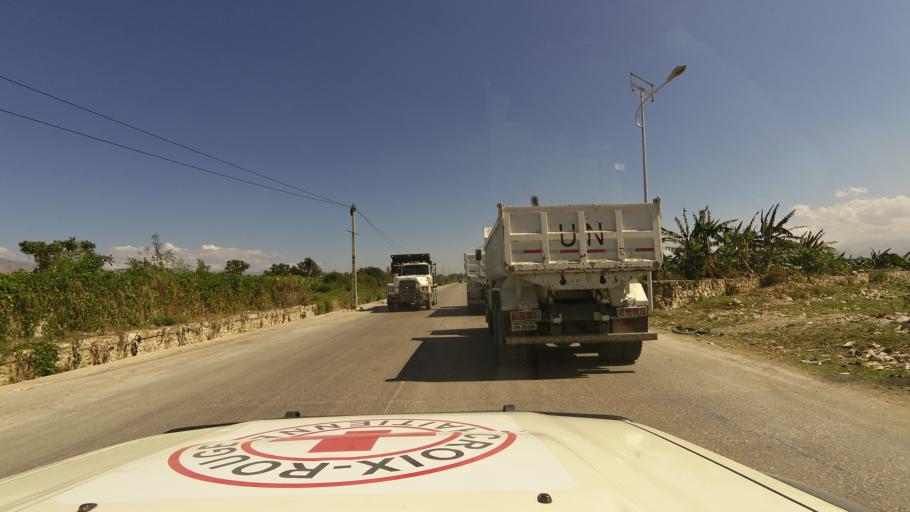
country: HT
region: Ouest
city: Delmas 73
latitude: 18.5902
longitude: -72.3256
